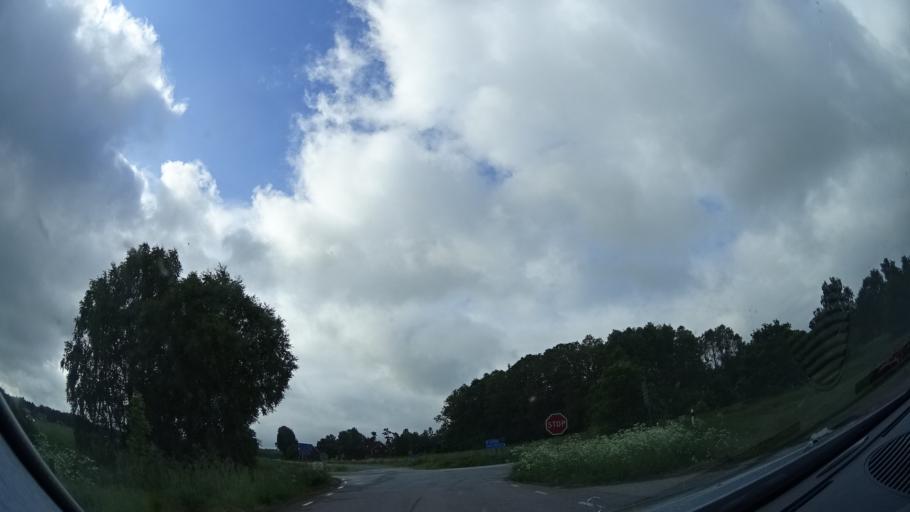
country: SE
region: Skane
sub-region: Eslovs Kommun
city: Stehag
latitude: 55.9489
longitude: 13.4524
